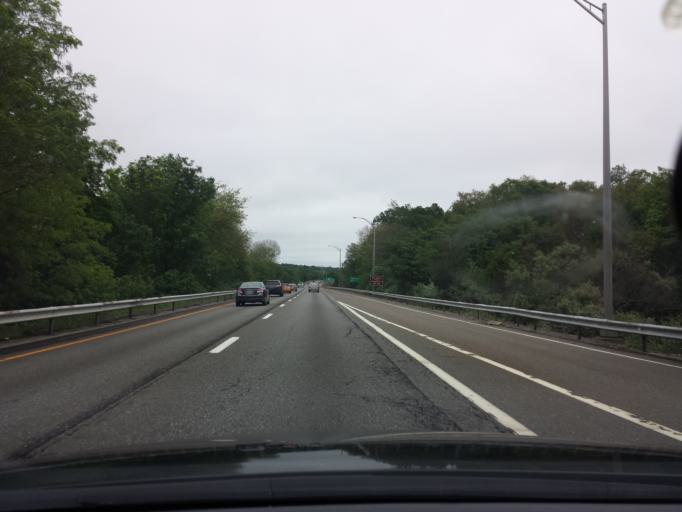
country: US
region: Connecticut
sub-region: New London County
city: Mystic
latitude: 41.3719
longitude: -71.9690
